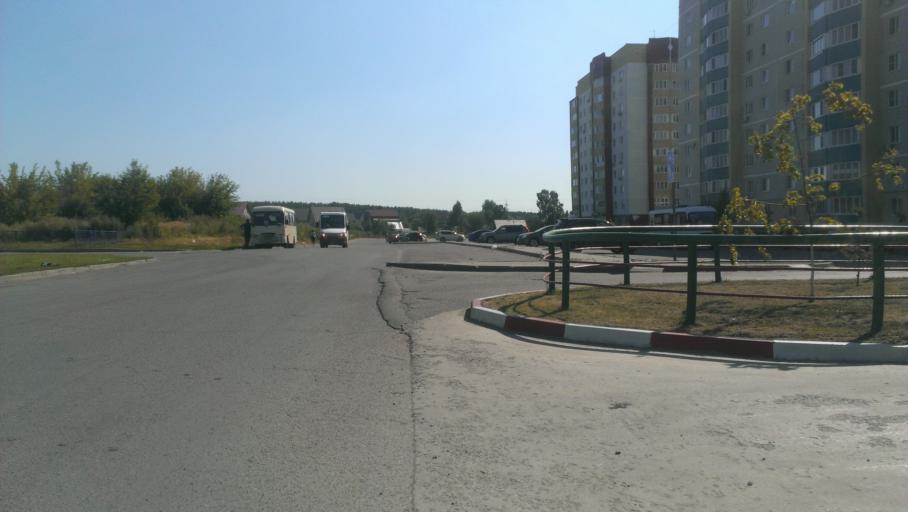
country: RU
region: Altai Krai
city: Novosilikatnyy
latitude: 53.3263
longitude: 83.6831
